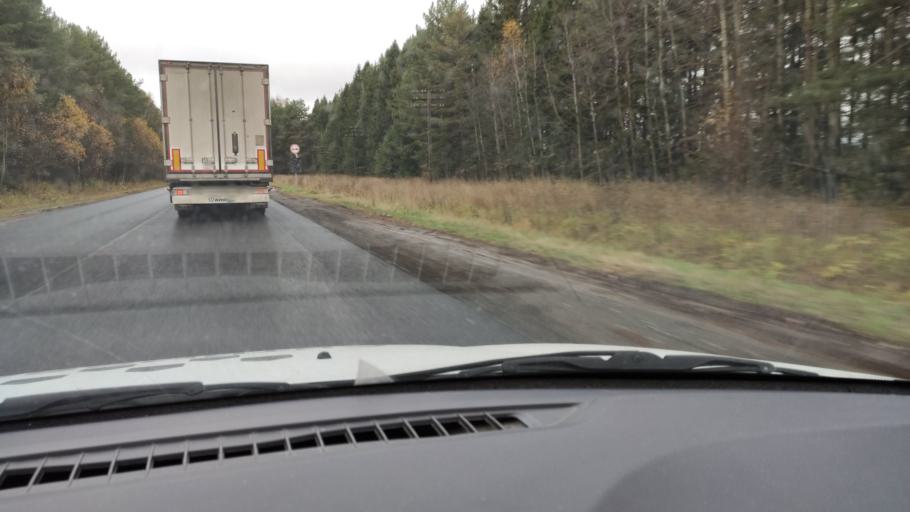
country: RU
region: Kirov
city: Slobodskoy
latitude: 58.7801
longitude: 50.4516
